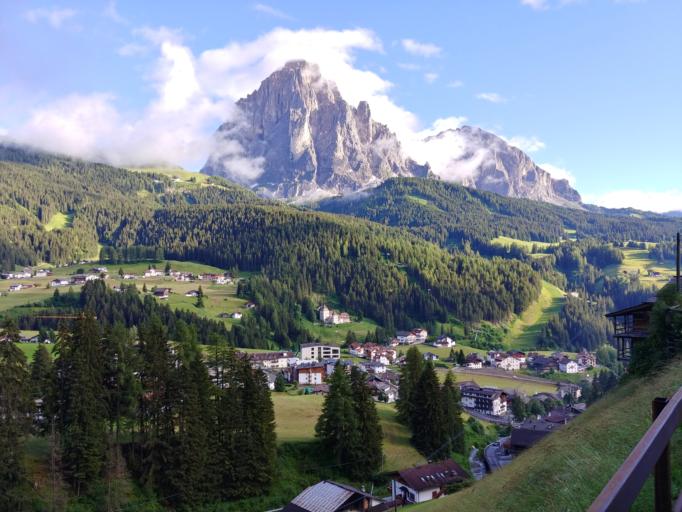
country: IT
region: Trentino-Alto Adige
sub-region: Bolzano
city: Santa Cristina Valgardena
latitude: 46.5654
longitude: 11.7345
